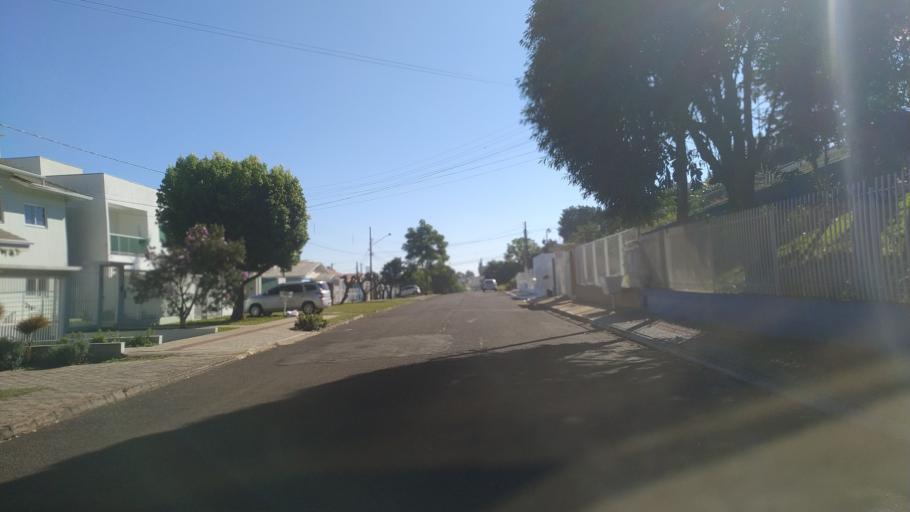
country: BR
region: Santa Catarina
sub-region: Chapeco
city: Chapeco
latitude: -27.1111
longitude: -52.6014
